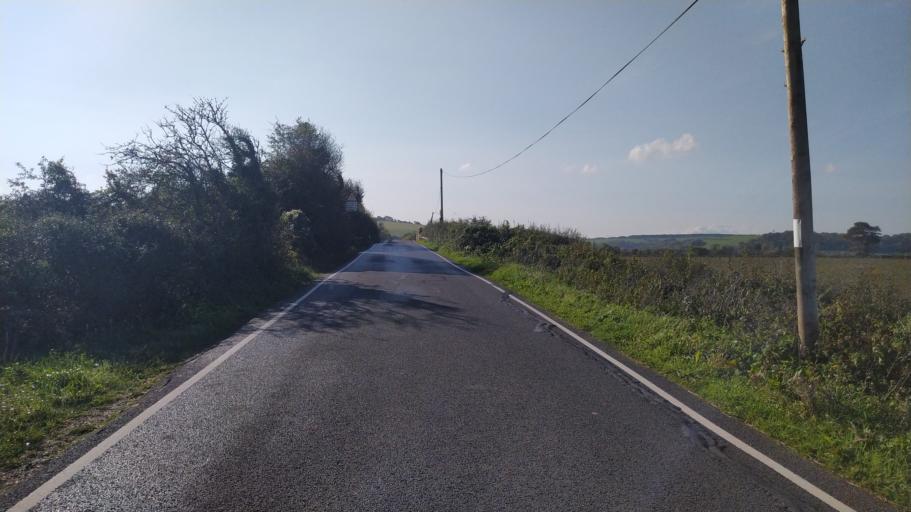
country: GB
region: England
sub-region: Isle of Wight
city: Newport
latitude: 50.6968
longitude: -1.3465
